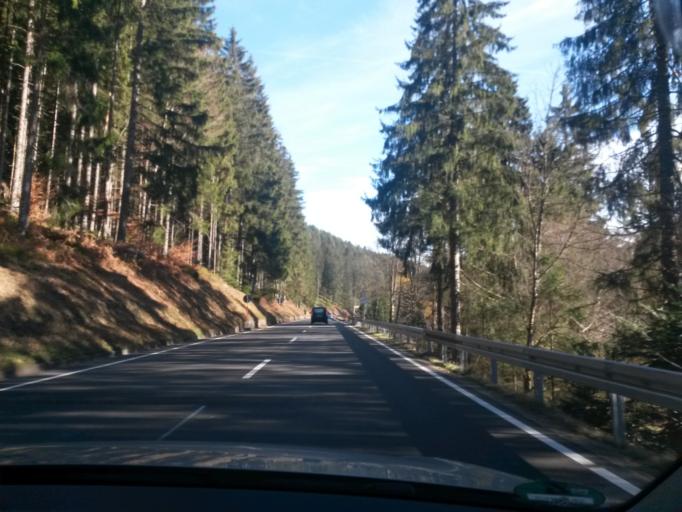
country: DE
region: Baden-Wuerttemberg
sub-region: Karlsruhe Region
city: Freudenstadt
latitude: 48.4562
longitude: 8.3797
